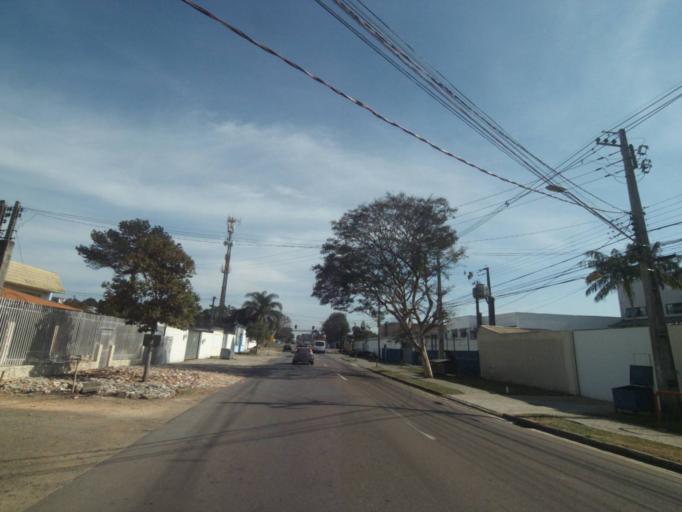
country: BR
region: Parana
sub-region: Sao Jose Dos Pinhais
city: Sao Jose dos Pinhais
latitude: -25.5109
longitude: -49.2317
